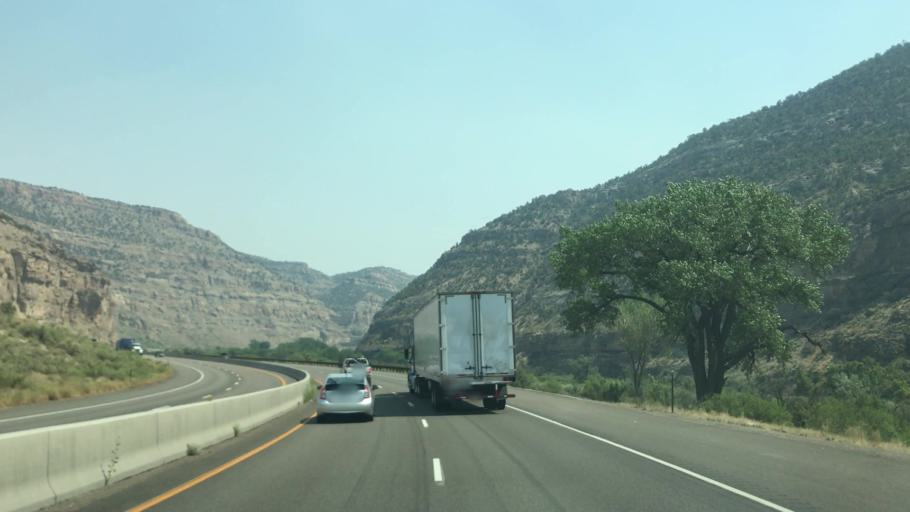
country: US
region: Colorado
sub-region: Mesa County
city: Palisade
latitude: 39.2311
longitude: -108.2711
